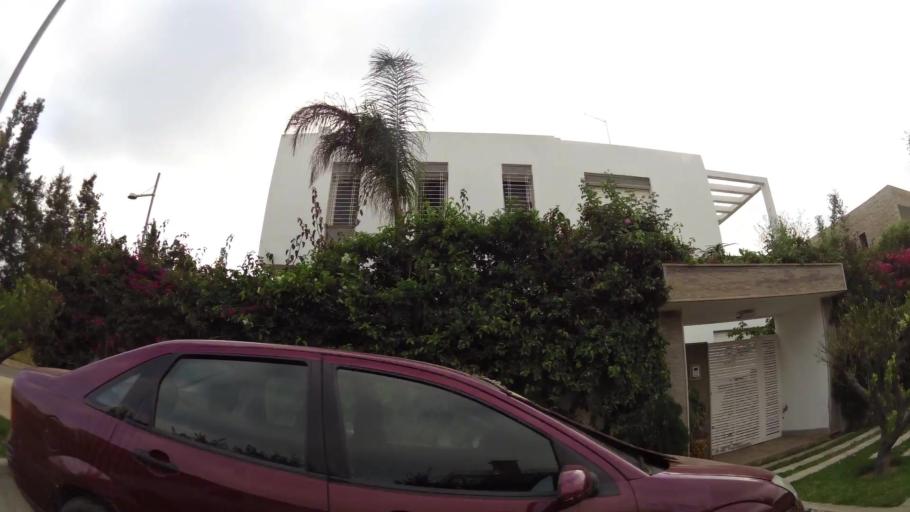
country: MA
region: Rabat-Sale-Zemmour-Zaer
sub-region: Rabat
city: Rabat
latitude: 33.9534
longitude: -6.8379
